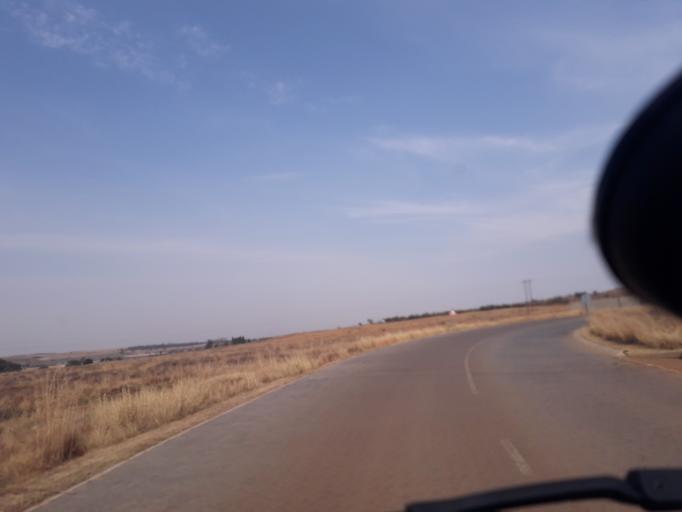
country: ZA
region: Gauteng
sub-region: West Rand District Municipality
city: Krugersdorp
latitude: -25.9762
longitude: 27.6635
